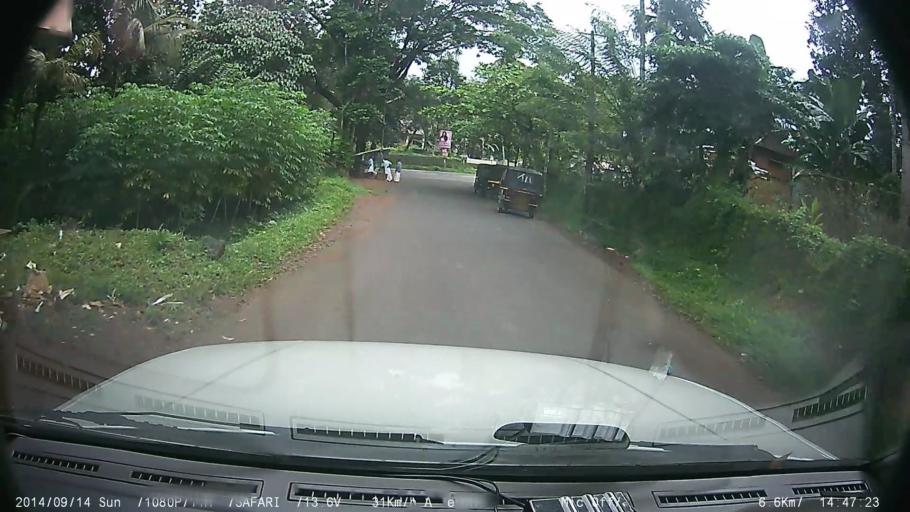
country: IN
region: Kerala
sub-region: Kottayam
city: Palackattumala
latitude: 9.7802
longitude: 76.5755
